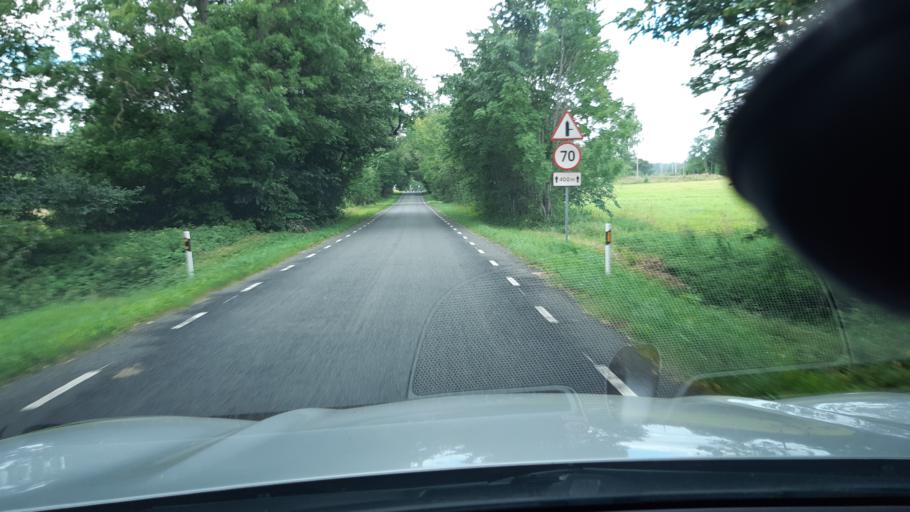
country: EE
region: Raplamaa
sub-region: Jaervakandi vald
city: Jarvakandi
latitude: 58.8748
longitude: 24.7537
